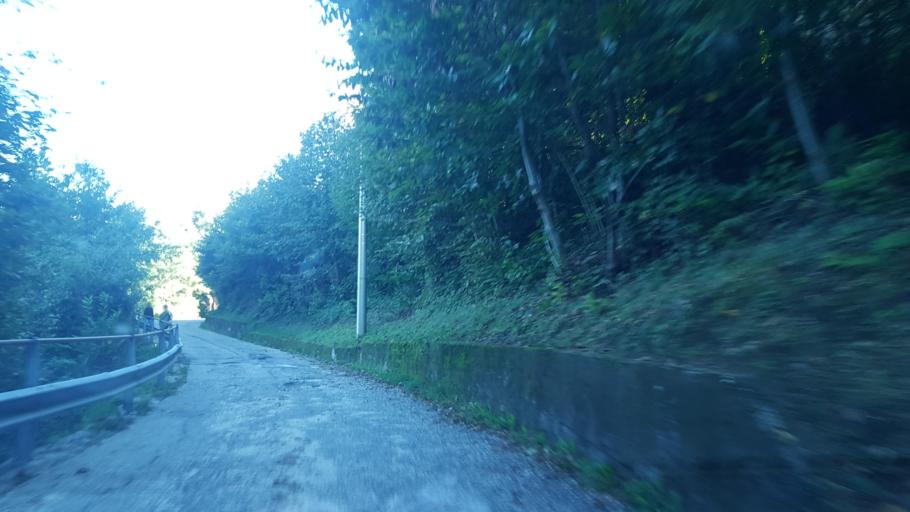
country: IT
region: Piedmont
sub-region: Provincia Verbano-Cusio-Ossola
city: Mergozzo
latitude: 45.9459
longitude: 8.4666
